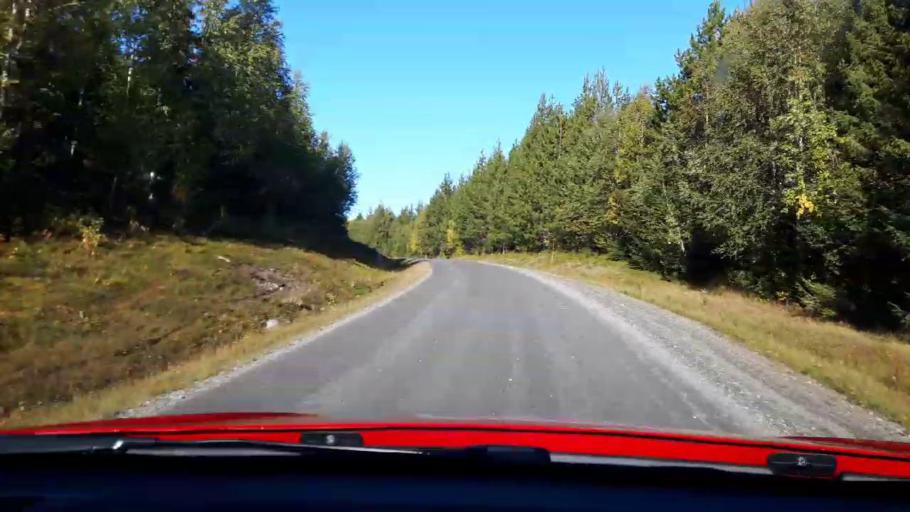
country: NO
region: Nord-Trondelag
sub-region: Lierne
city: Sandvika
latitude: 64.5329
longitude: 14.0348
